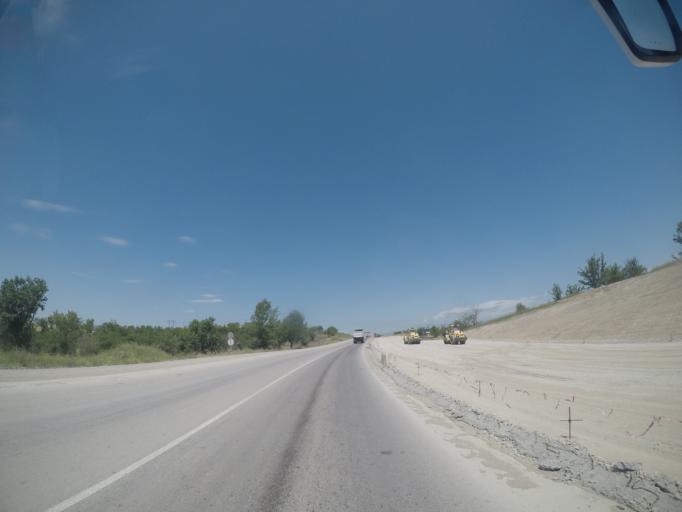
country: AZ
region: Qobustan
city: Qobustan
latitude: 40.5313
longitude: 48.7843
